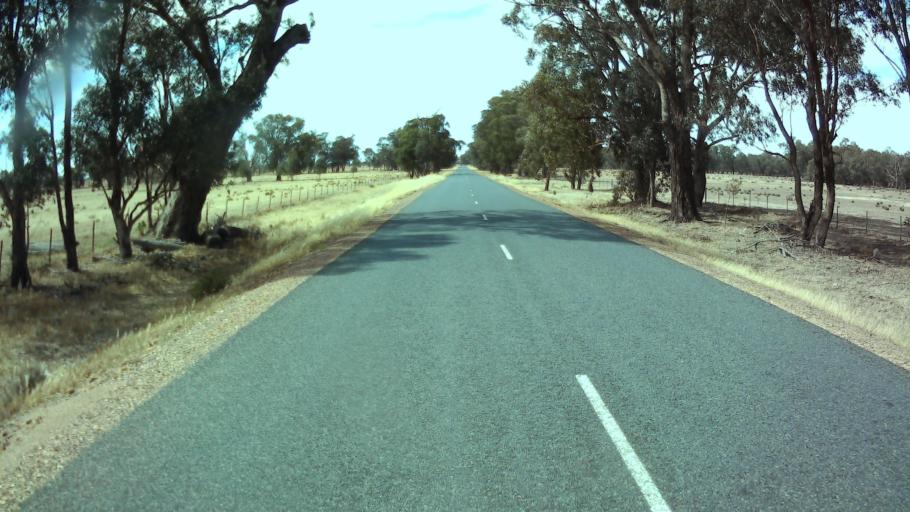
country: AU
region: New South Wales
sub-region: Weddin
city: Grenfell
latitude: -33.7607
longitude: 148.2159
